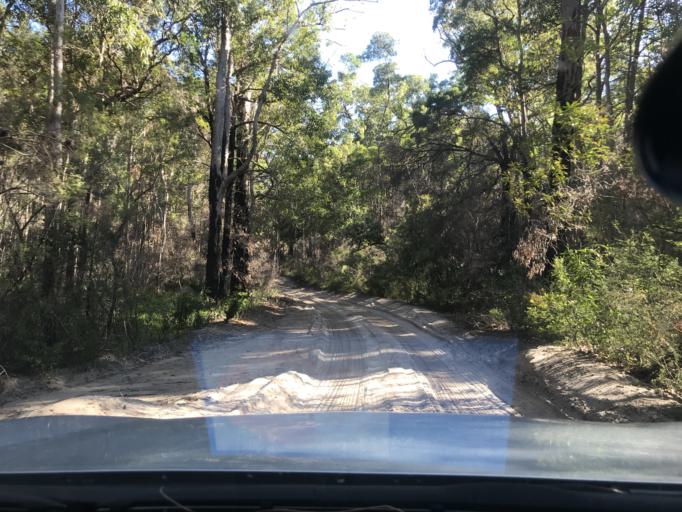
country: AU
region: Queensland
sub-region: Fraser Coast
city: Urangan
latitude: -25.4988
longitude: 153.0993
